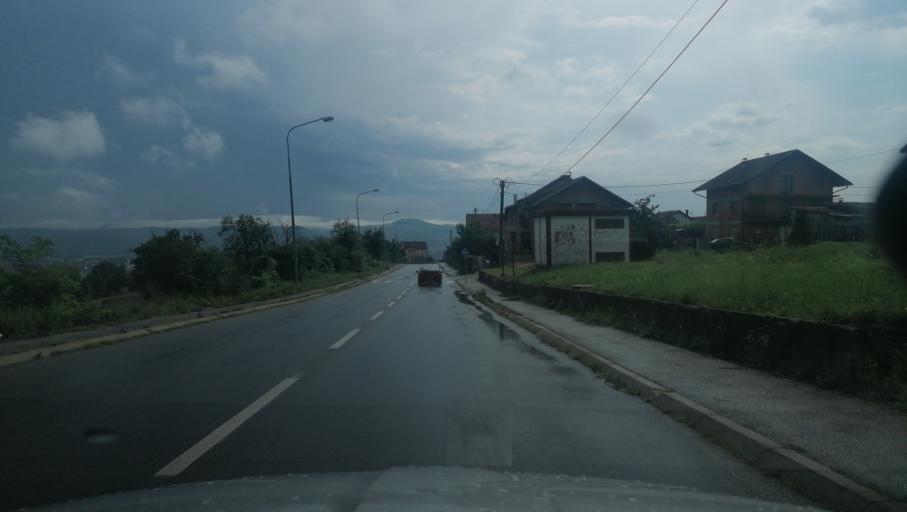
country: BA
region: Republika Srpska
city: Banja Luka
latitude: 44.7903
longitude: 17.1777
